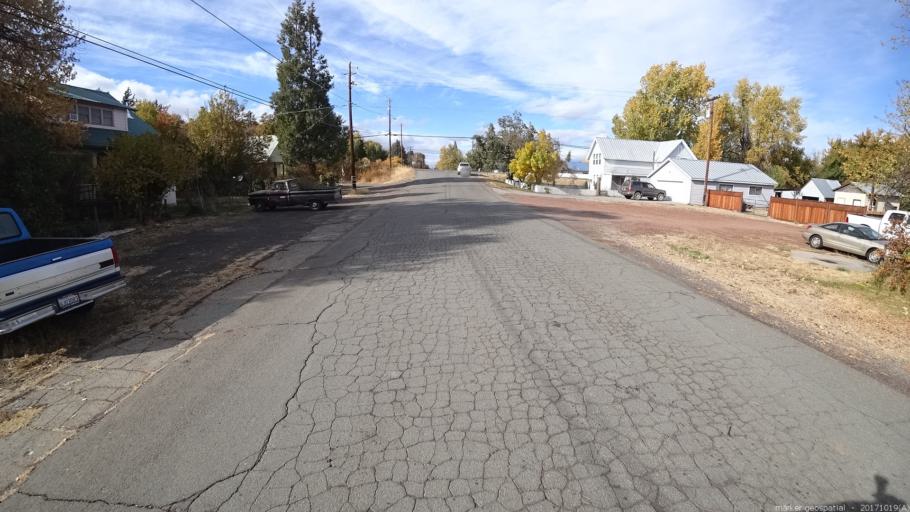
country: US
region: California
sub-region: Shasta County
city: Burney
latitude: 41.0020
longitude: -121.4425
